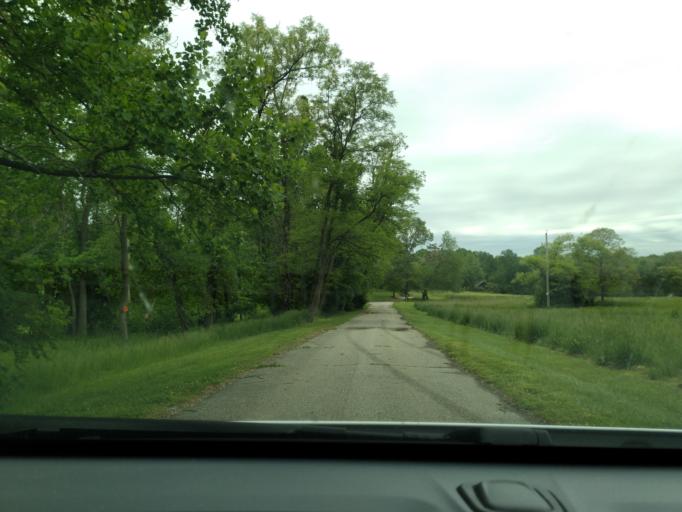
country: US
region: Maryland
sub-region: Prince George's County
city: Marlboro Meadows
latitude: 38.8599
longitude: -76.7091
